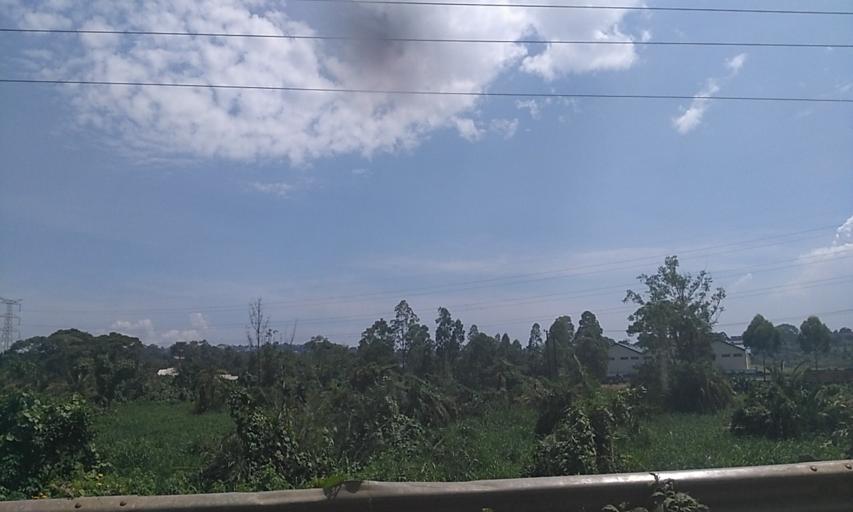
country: UG
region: Central Region
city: Kampala Central Division
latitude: 0.4042
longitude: 32.5870
